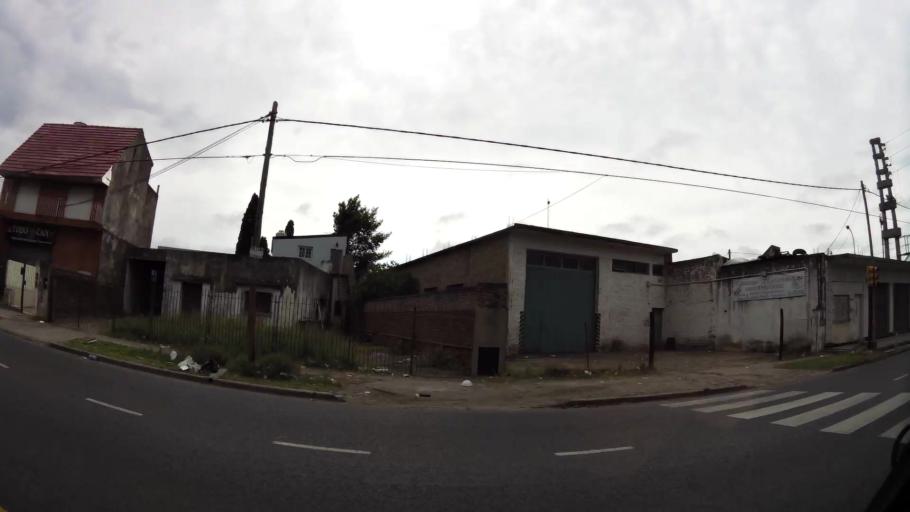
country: AR
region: Buenos Aires
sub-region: Partido de Quilmes
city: Quilmes
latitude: -34.7503
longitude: -58.2909
